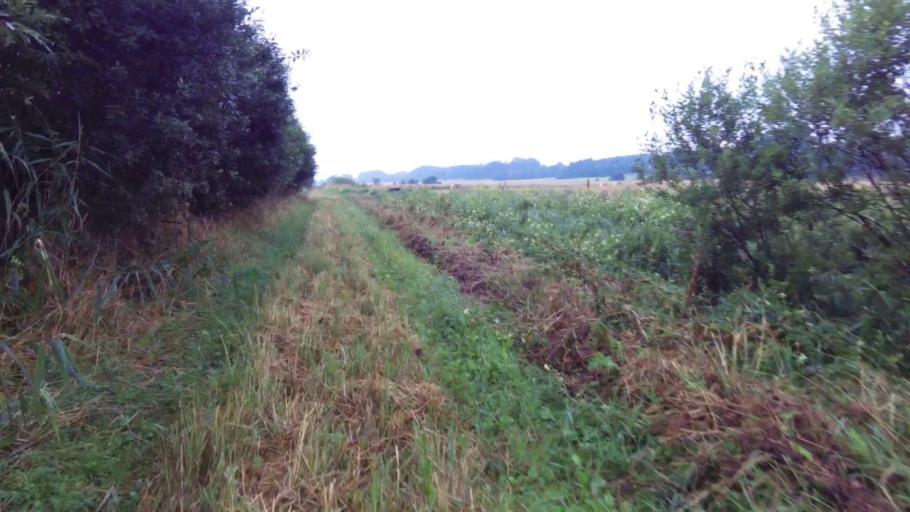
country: PL
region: West Pomeranian Voivodeship
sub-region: Powiat choszczenski
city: Choszczno
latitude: 53.2494
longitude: 15.4133
